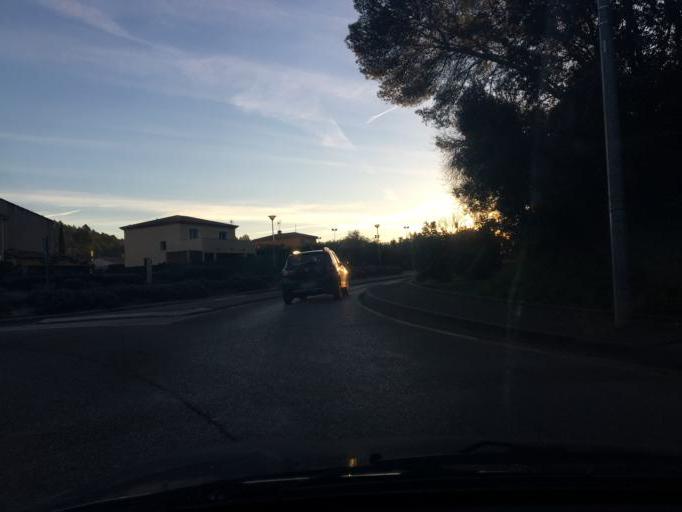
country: FR
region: Provence-Alpes-Cote d'Azur
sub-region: Departement du Var
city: Taradeau
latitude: 43.4518
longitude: 6.4296
